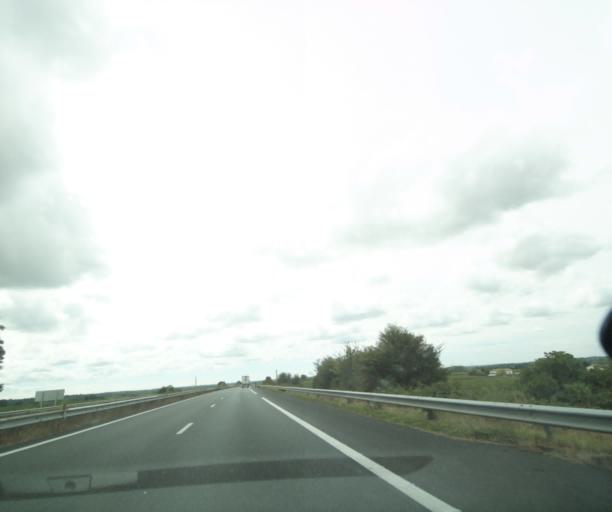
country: FR
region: Aquitaine
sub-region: Departement de la Gironde
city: Marcillac
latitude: 45.2877
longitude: -0.5517
